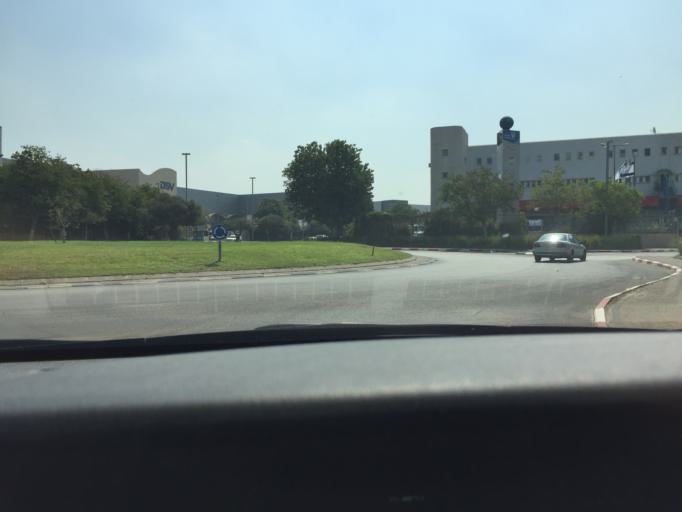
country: IL
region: Central District
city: Yehud
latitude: 31.9902
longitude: 34.9146
